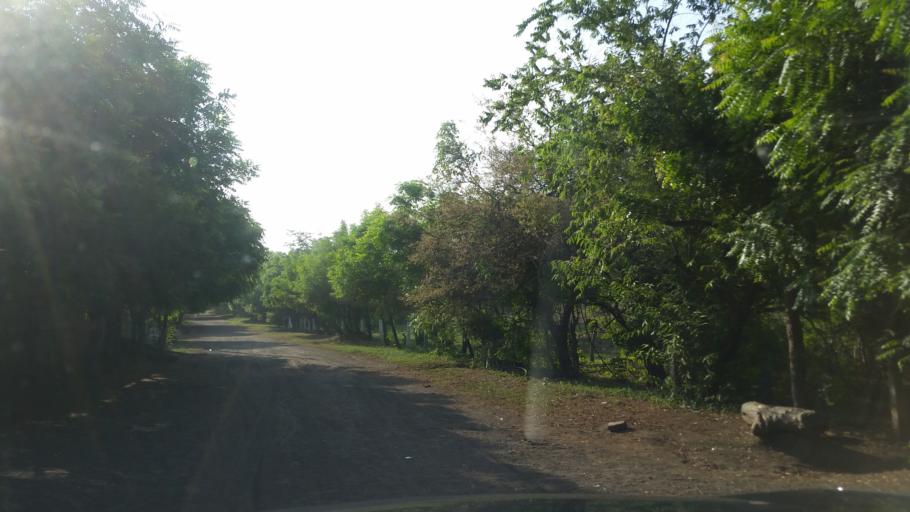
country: NI
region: Managua
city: Masachapa
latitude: 11.7549
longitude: -86.4862
